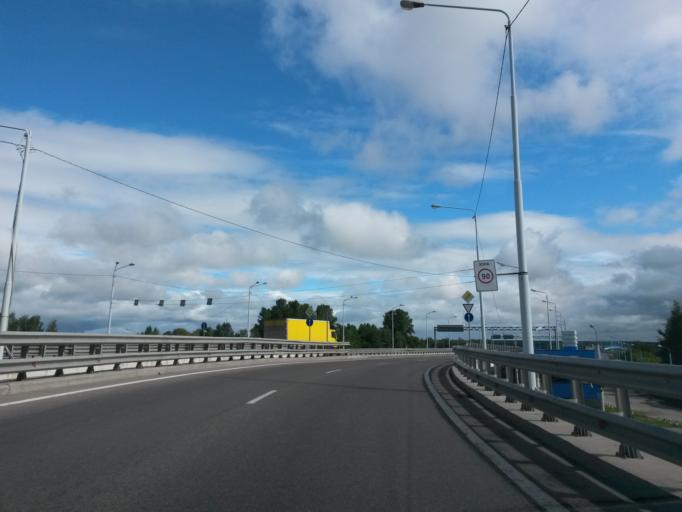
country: RU
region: Jaroslavl
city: Yaroslavl
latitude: 57.6685
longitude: 39.8409
